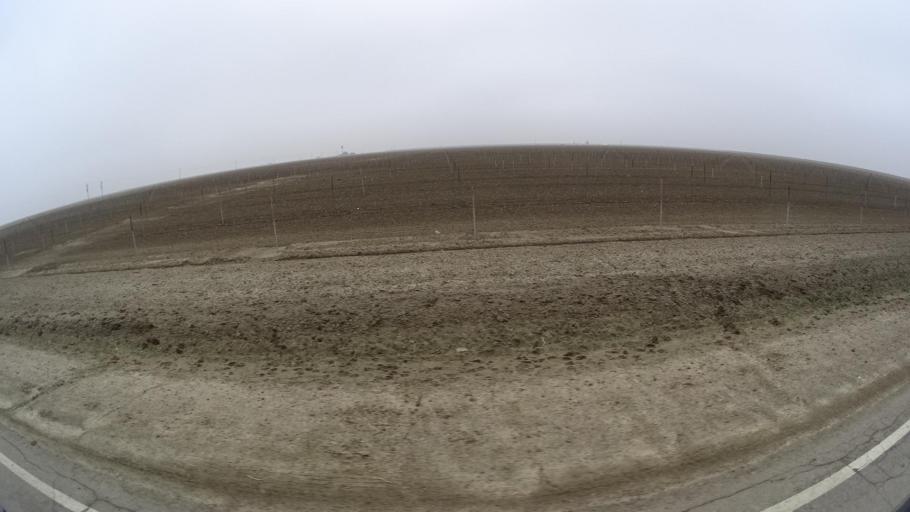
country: US
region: California
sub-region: Tulare County
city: Alpaugh
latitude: 35.7008
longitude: -119.5085
